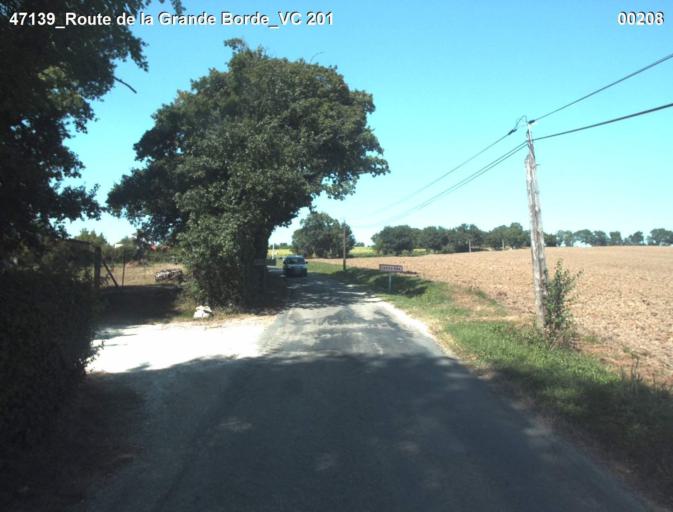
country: FR
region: Aquitaine
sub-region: Departement du Lot-et-Garonne
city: Nerac
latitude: 44.0640
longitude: 0.3933
